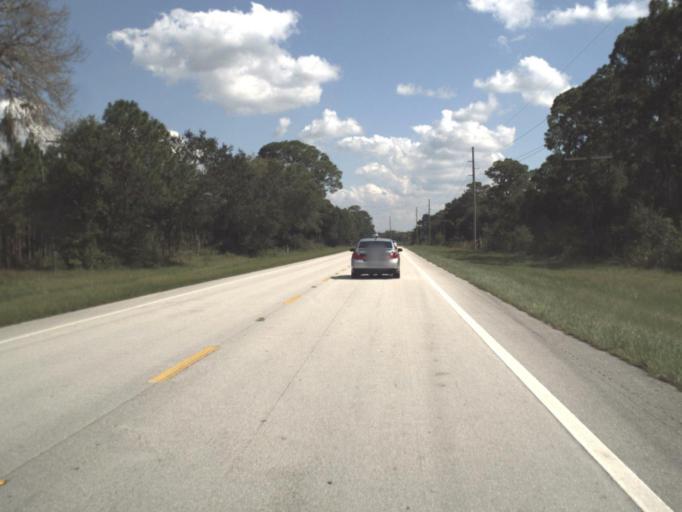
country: US
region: Florida
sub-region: Okeechobee County
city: Okeechobee
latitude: 27.3642
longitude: -81.0622
